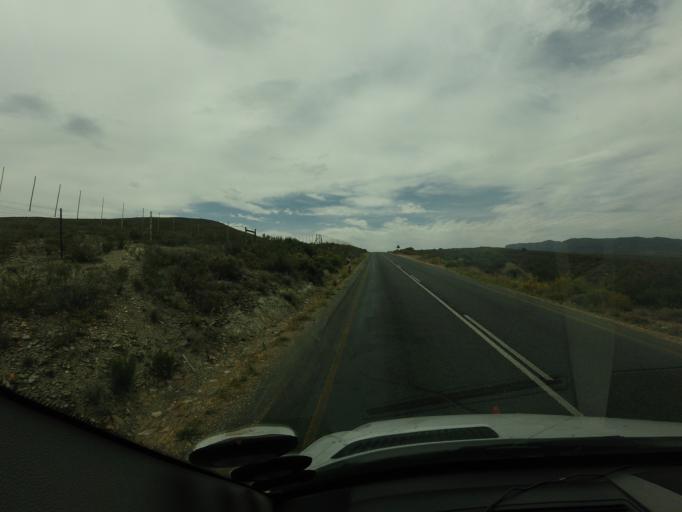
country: ZA
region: Western Cape
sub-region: Overberg District Municipality
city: Swellendam
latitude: -33.8914
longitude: 20.7286
